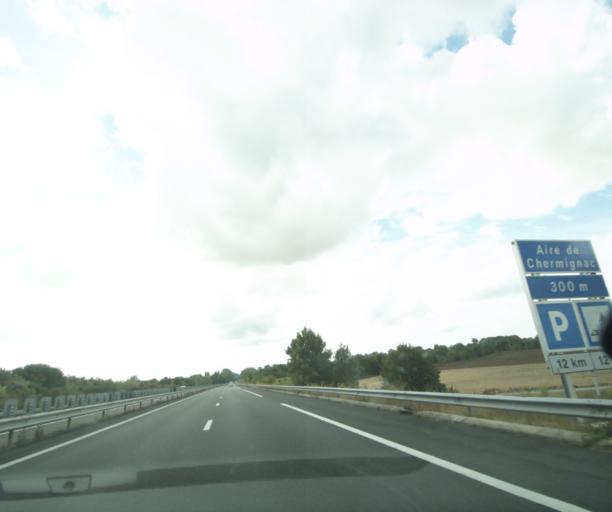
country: FR
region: Poitou-Charentes
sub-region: Departement de la Charente-Maritime
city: Chermignac
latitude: 45.7103
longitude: -0.6550
